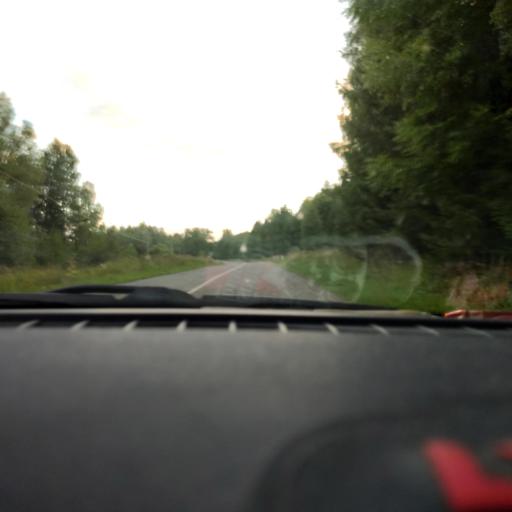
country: RU
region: Perm
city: Ocher
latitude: 57.9376
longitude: 54.8027
